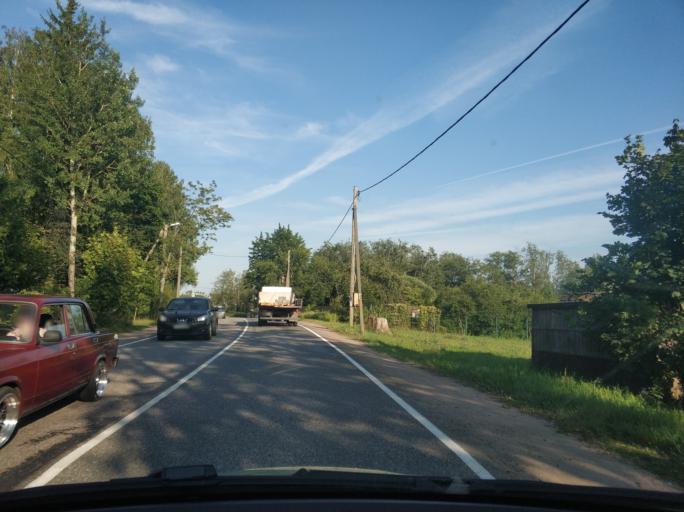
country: RU
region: Leningrad
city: Borisova Griva
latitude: 60.0949
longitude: 30.9708
